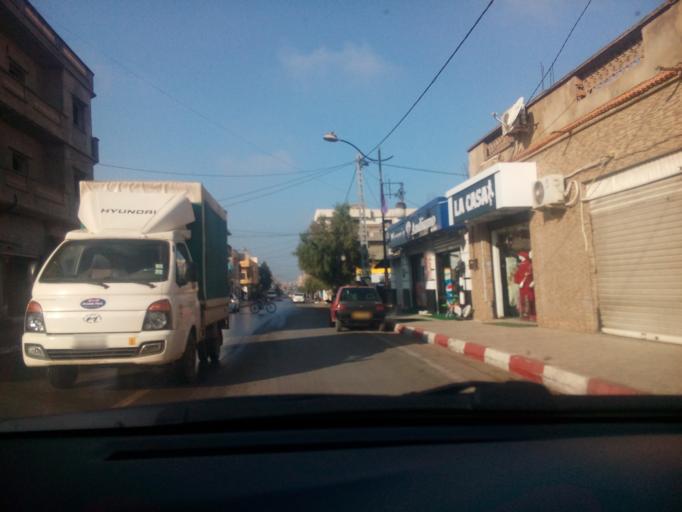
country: DZ
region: Oran
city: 'Ain el Turk
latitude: 35.7368
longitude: -0.7476
